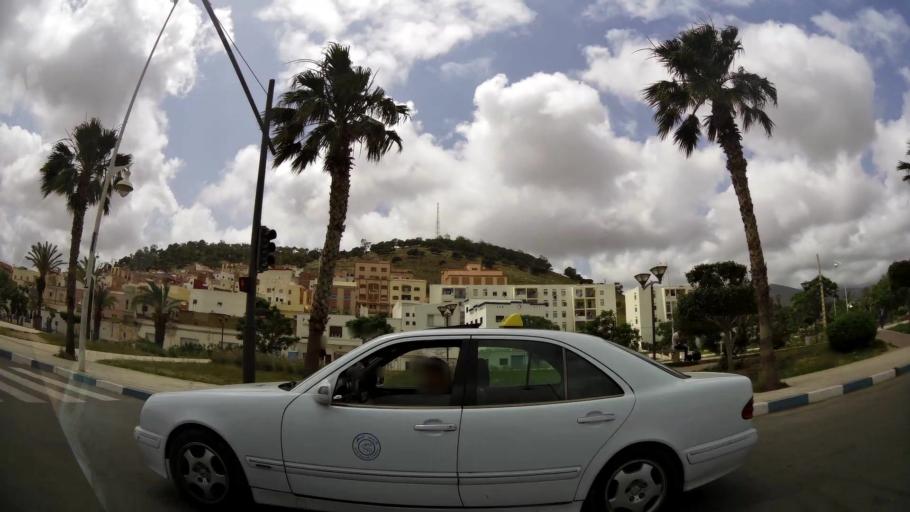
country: MA
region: Oriental
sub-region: Nador
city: Nador
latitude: 35.1828
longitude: -2.9270
